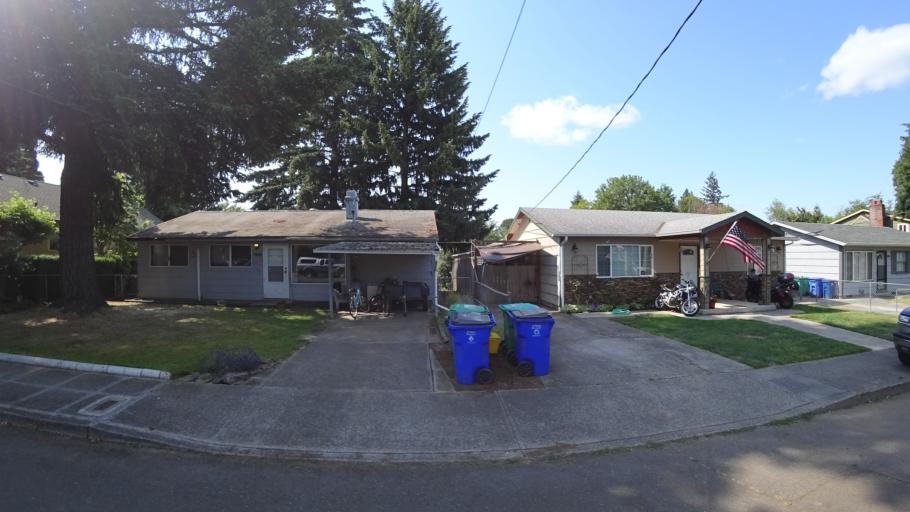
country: US
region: Washington
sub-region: Clark County
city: Vancouver
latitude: 45.5991
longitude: -122.7360
